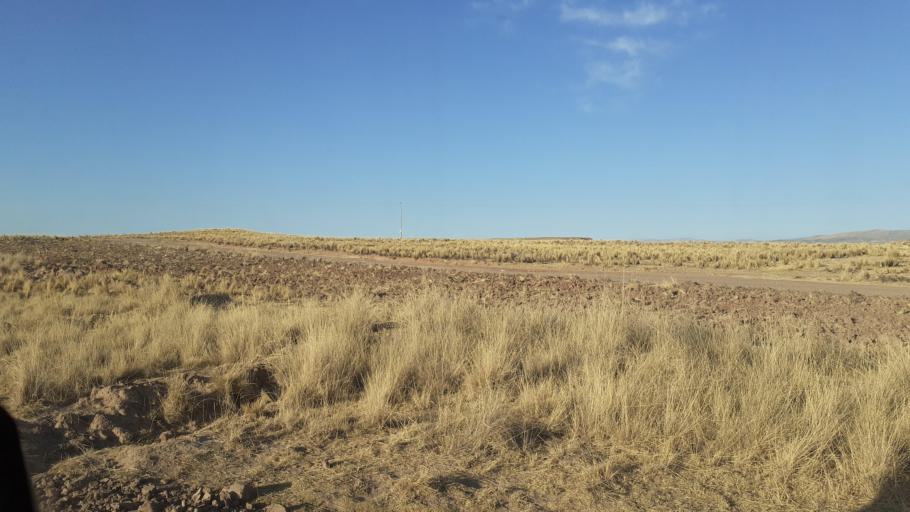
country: BO
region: La Paz
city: Tiahuanaco
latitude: -16.9524
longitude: -68.7603
